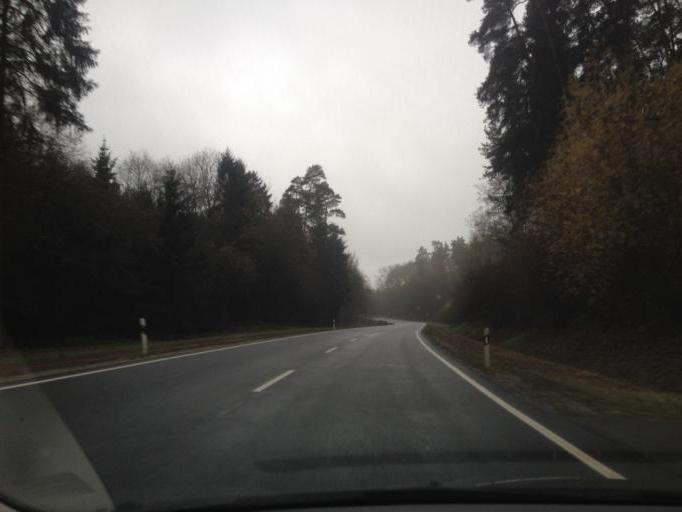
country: DE
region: Bavaria
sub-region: Regierungsbezirk Mittelfranken
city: Heroldsberg
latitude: 49.5512
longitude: 11.1662
